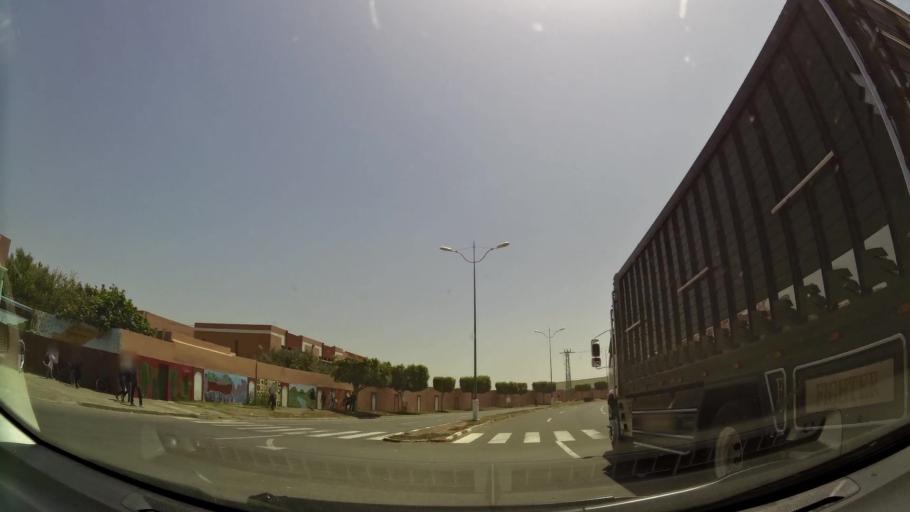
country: MA
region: Souss-Massa-Draa
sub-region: Inezgane-Ait Mellou
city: Inezgane
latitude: 30.3429
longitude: -9.4828
